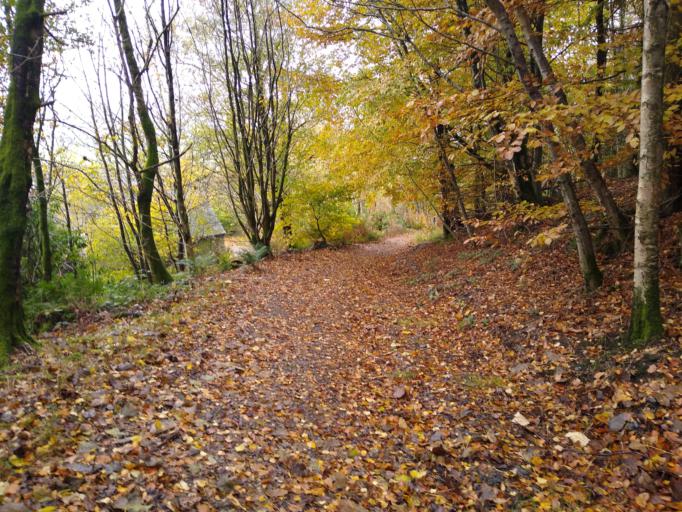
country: GB
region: England
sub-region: Cumbria
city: Keswick
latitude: 54.6209
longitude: -3.0807
